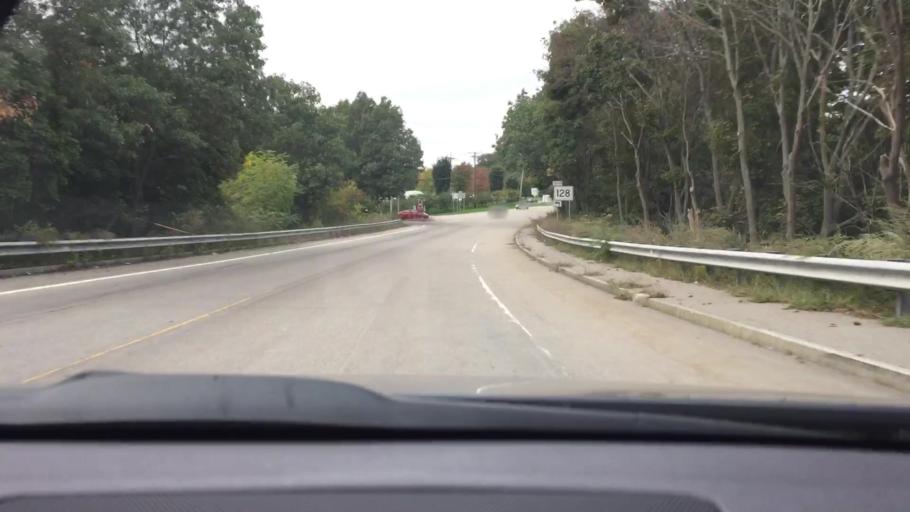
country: US
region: Massachusetts
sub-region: Norfolk County
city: Needham
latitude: 42.2697
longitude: -71.2018
